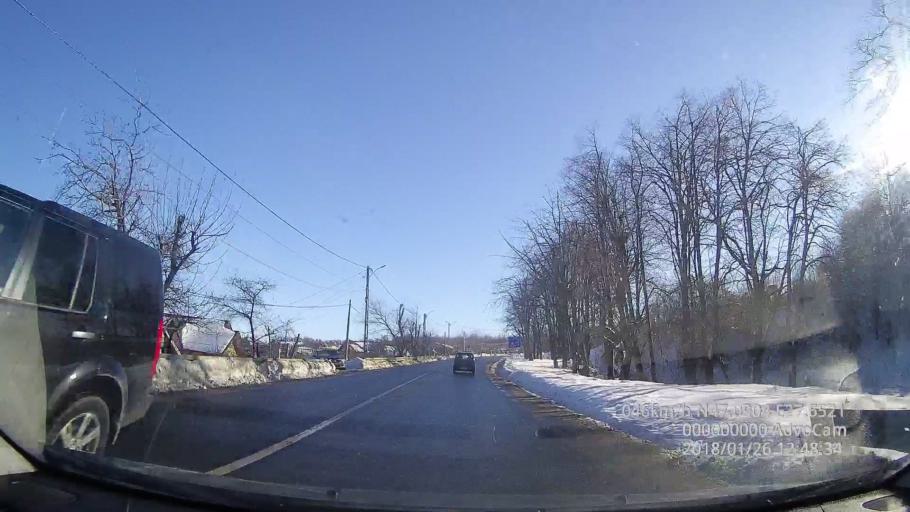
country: RO
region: Iasi
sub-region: Comuna Tomesti
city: Tomesti
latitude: 47.0904
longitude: 27.6527
